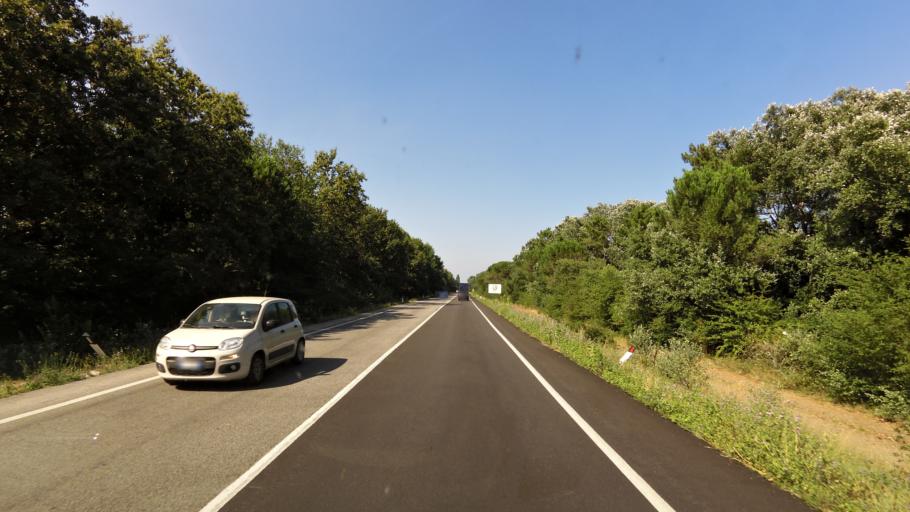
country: IT
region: Emilia-Romagna
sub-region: Provincia di Ravenna
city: Marina Romea
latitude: 44.5004
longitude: 12.2188
